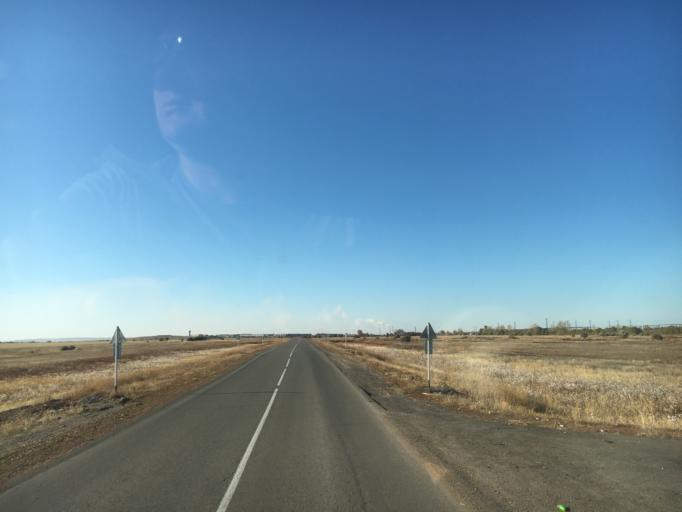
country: KZ
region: Qaraghandy
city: Aqtau
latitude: 50.1927
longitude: 73.0961
